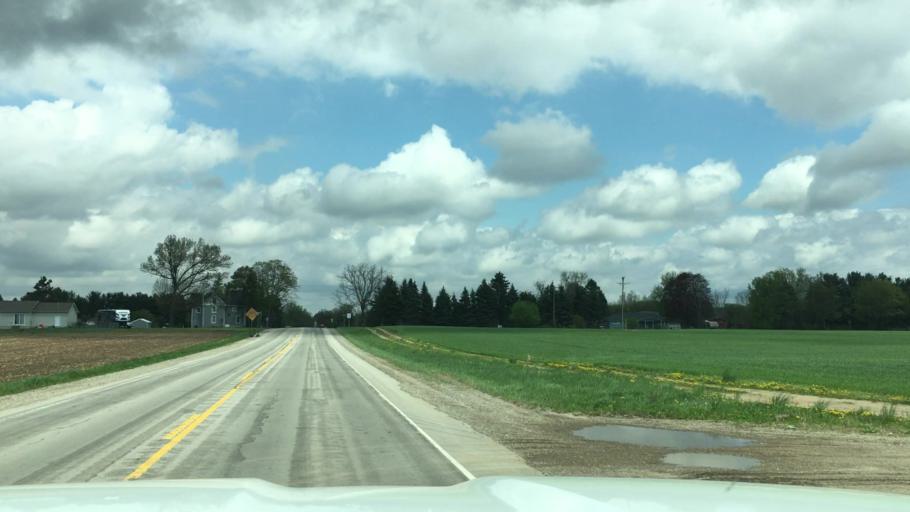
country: US
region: Michigan
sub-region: Ingham County
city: Stockbridge
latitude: 42.4666
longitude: -84.1901
